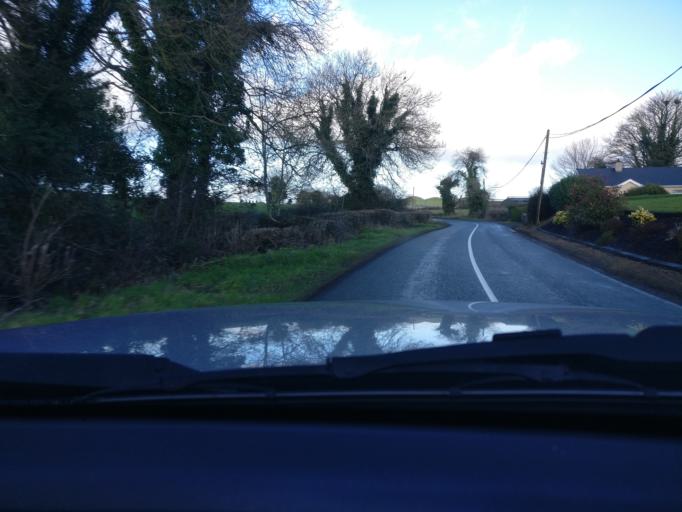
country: IE
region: Ulster
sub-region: An Cabhan
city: Mullagh
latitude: 53.7037
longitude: -7.0128
